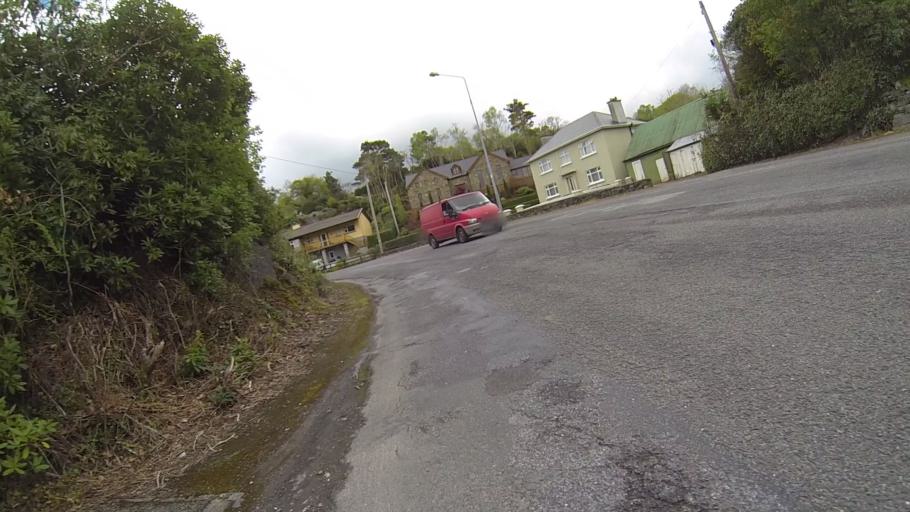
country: IE
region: Munster
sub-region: County Cork
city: Bantry
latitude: 51.7475
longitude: -9.5556
